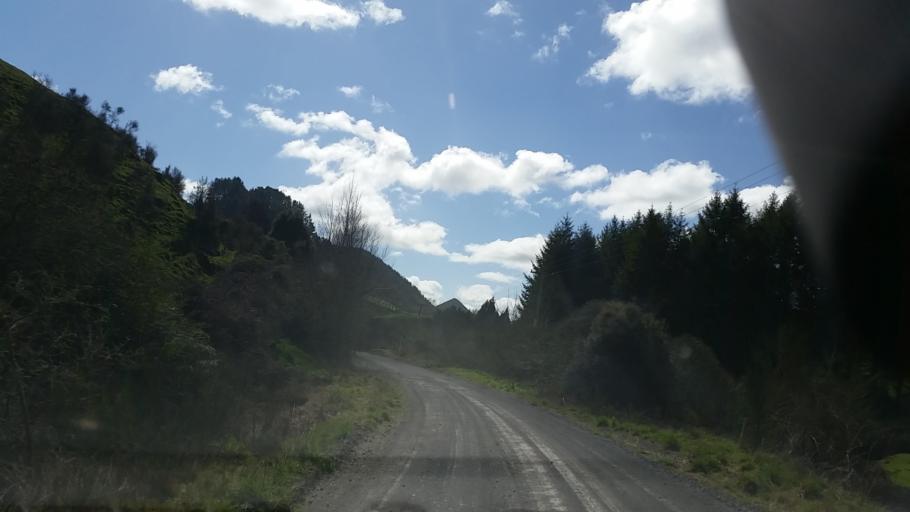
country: NZ
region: Waikato
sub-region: Taupo District
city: Taupo
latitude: -38.4733
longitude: 176.2246
